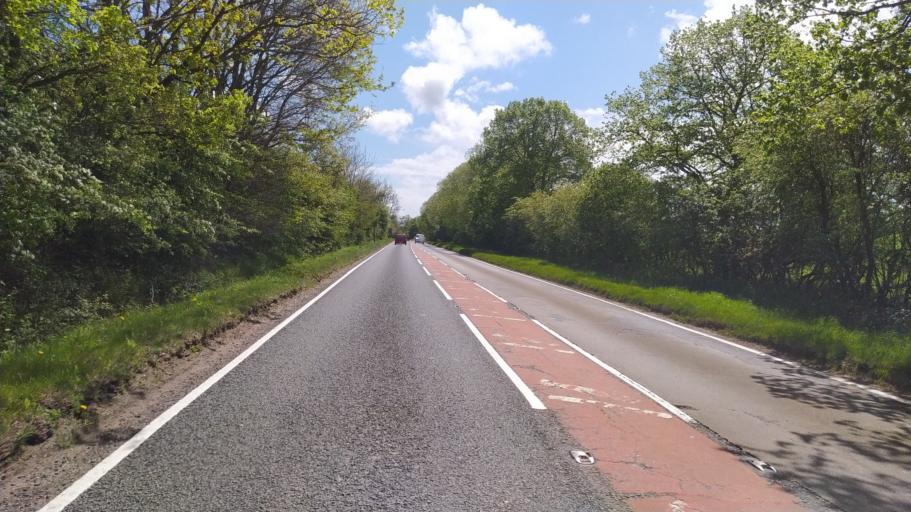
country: GB
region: England
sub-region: Hampshire
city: Ringwood
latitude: 50.8725
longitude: -1.7918
